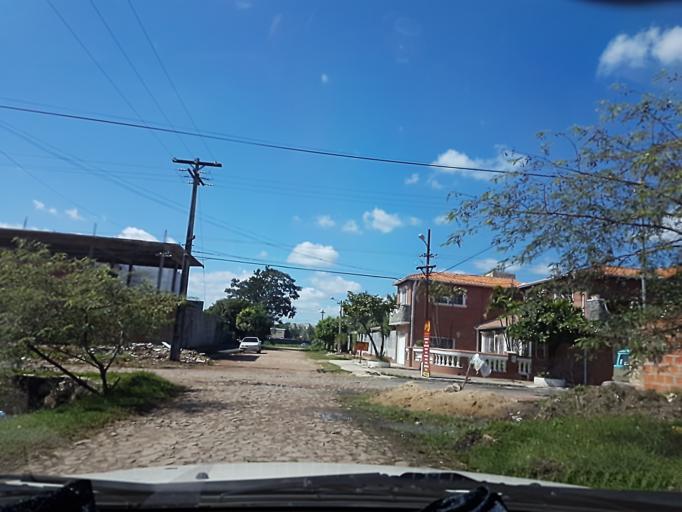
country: PY
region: Central
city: Colonia Mariano Roque Alonso
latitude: -25.2087
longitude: -57.5321
